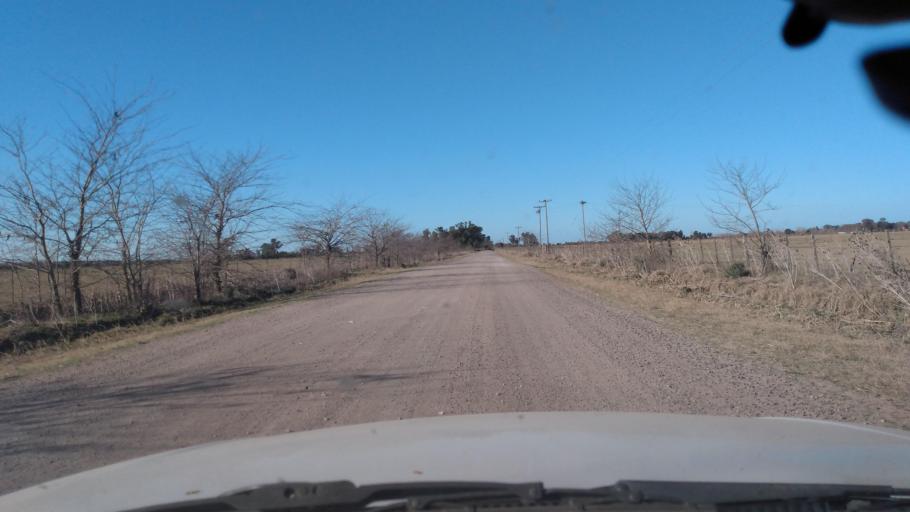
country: AR
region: Buenos Aires
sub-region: Partido de Mercedes
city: Mercedes
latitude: -34.6112
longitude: -59.3178
